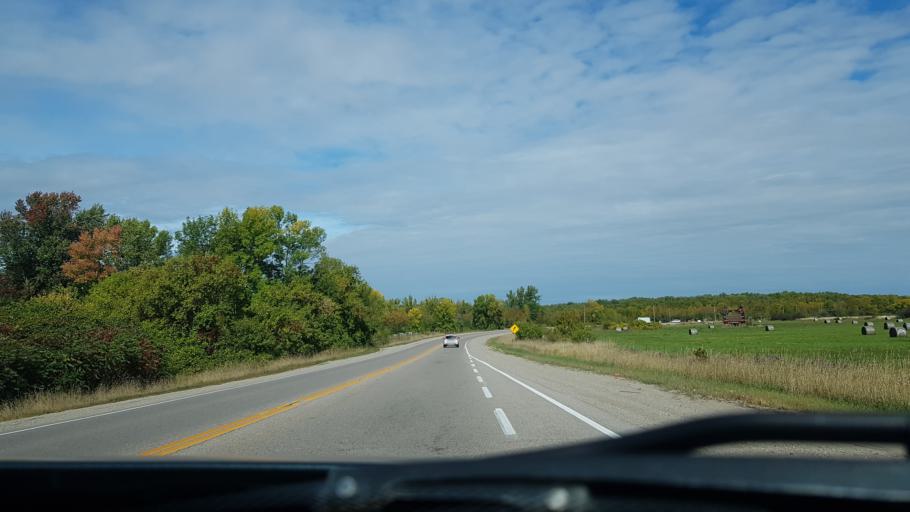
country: CA
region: Ontario
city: Orillia
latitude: 44.6058
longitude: -79.3581
